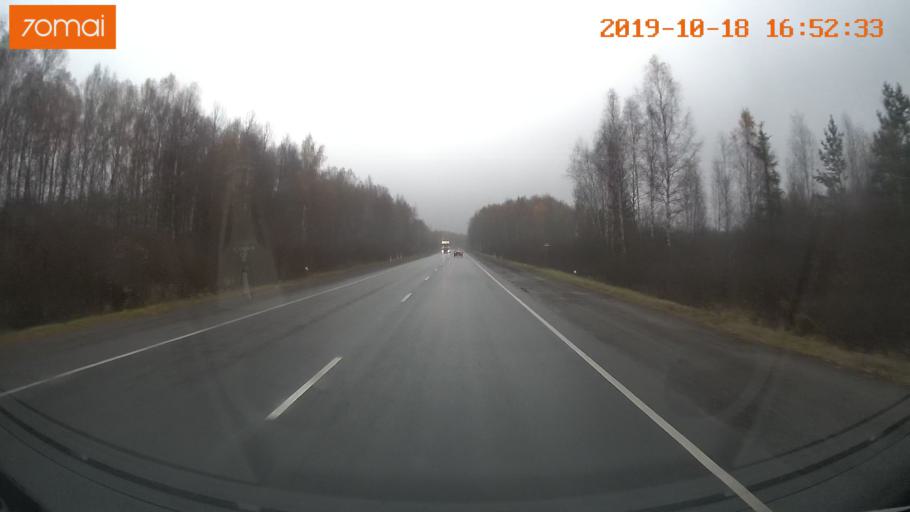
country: RU
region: Ivanovo
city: Nerl'
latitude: 56.6024
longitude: 40.5560
